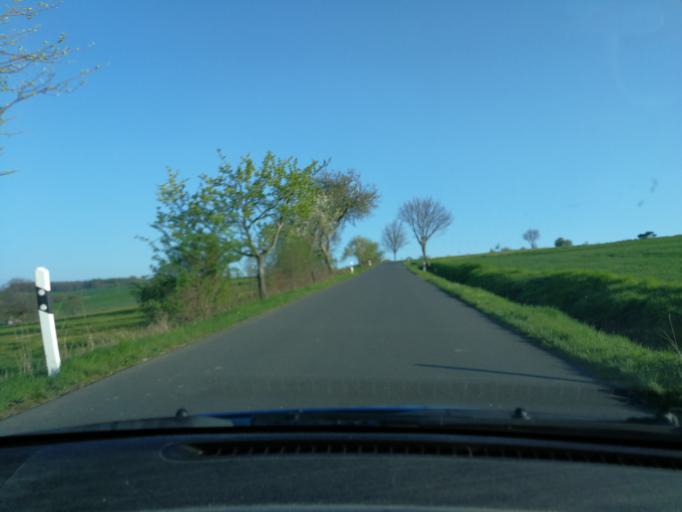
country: DE
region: Lower Saxony
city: Uslar
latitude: 51.6113
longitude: 9.6395
